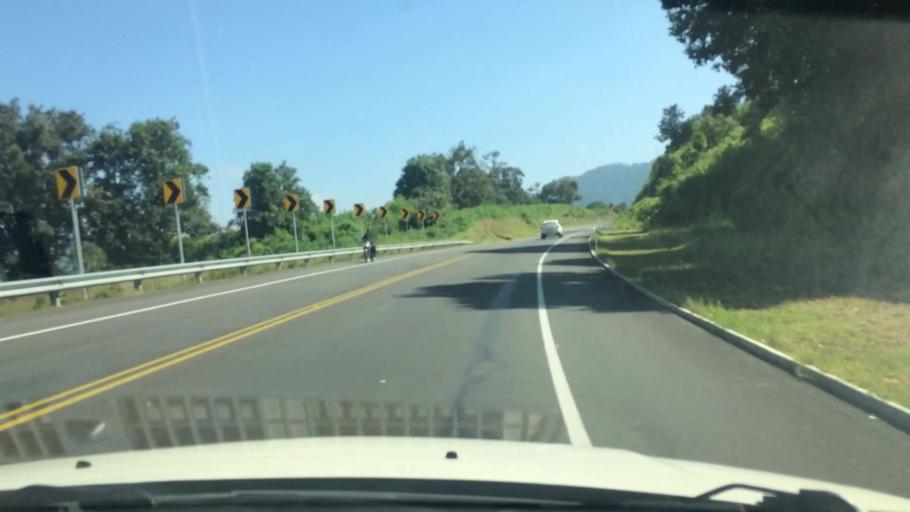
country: MX
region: Mexico
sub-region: Valle de Bravo
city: Colonia Rincon Villa del Valle
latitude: 19.2172
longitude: -100.0989
